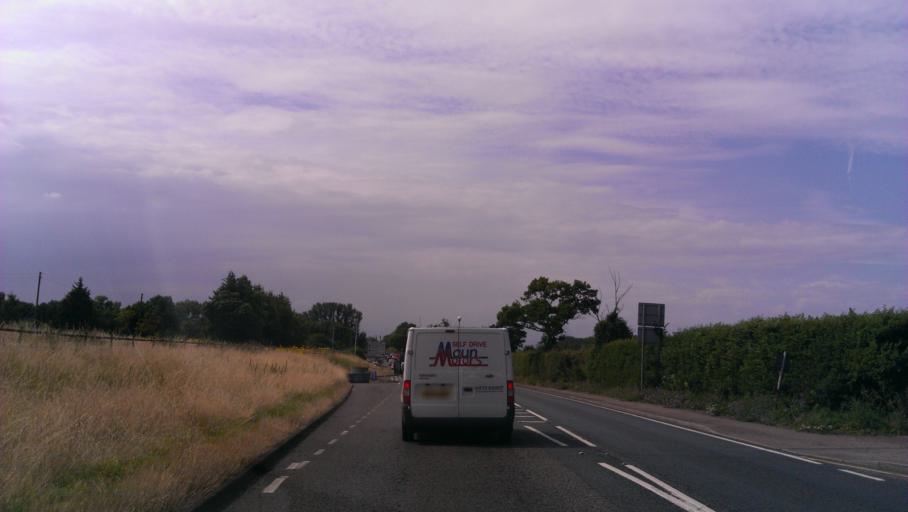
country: GB
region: England
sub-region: Kent
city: Teynham
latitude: 51.3206
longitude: 0.8285
